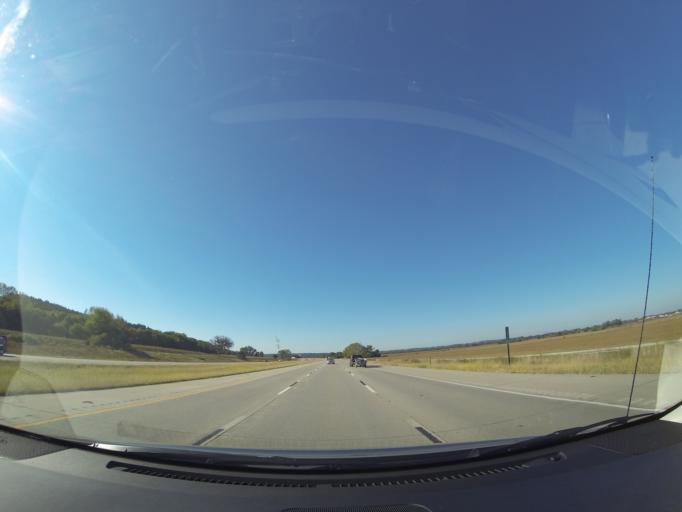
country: US
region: Nebraska
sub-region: Saunders County
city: Ashland
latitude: 41.0646
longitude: -96.2916
